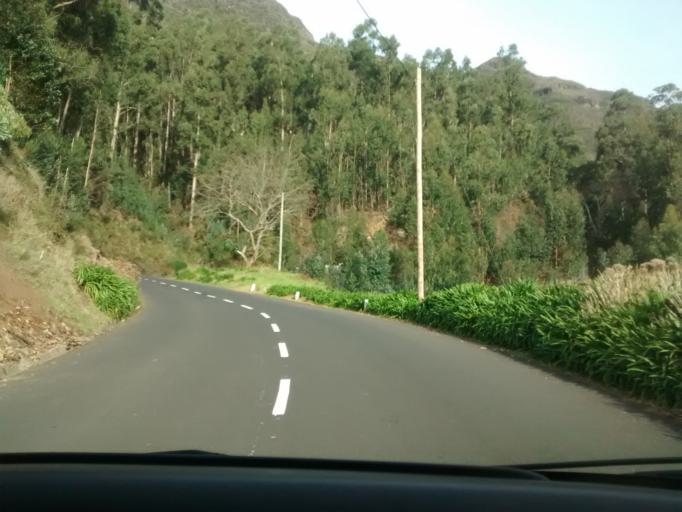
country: PT
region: Madeira
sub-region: Sao Vicente
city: Sao Vicente
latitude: 32.7452
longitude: -17.0250
